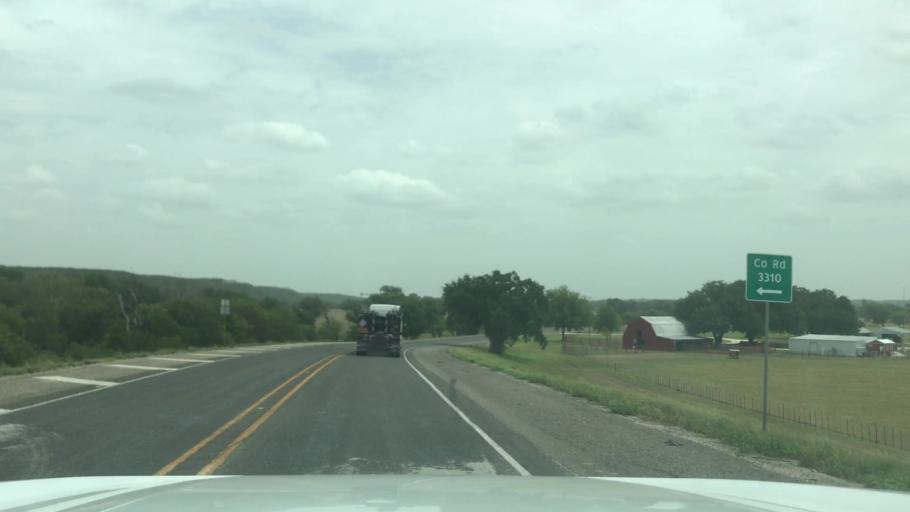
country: US
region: Texas
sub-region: Bosque County
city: Valley Mills
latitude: 31.6751
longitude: -97.5128
